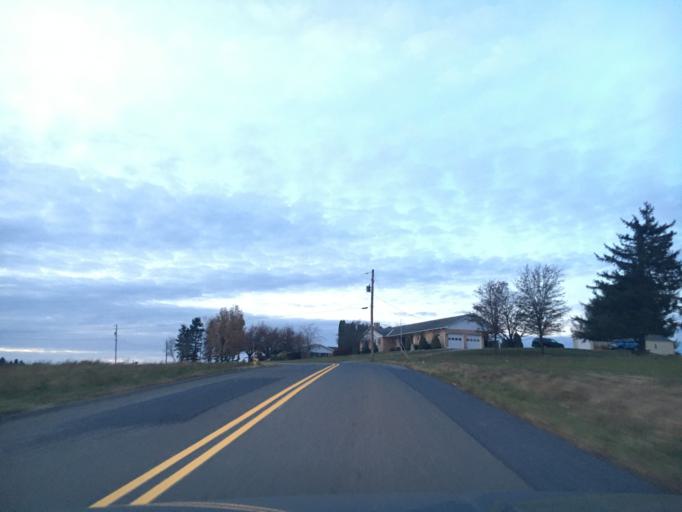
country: US
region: Pennsylvania
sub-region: Lehigh County
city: Schnecksville
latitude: 40.6889
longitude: -75.5735
